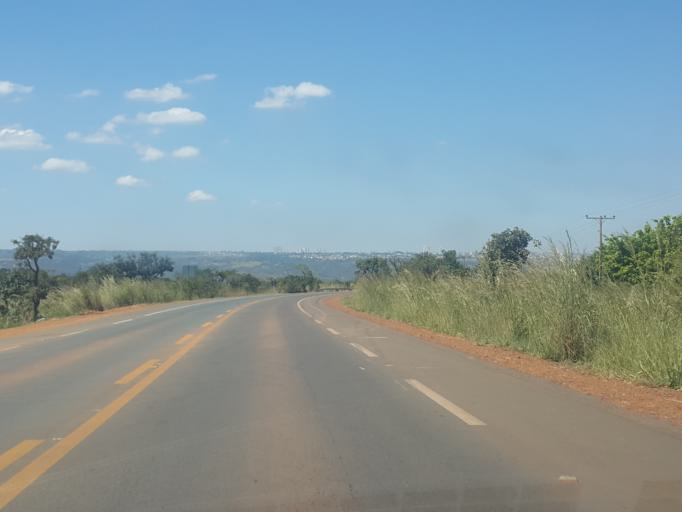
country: BR
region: Goias
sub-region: Luziania
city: Luziania
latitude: -16.0082
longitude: -48.1524
